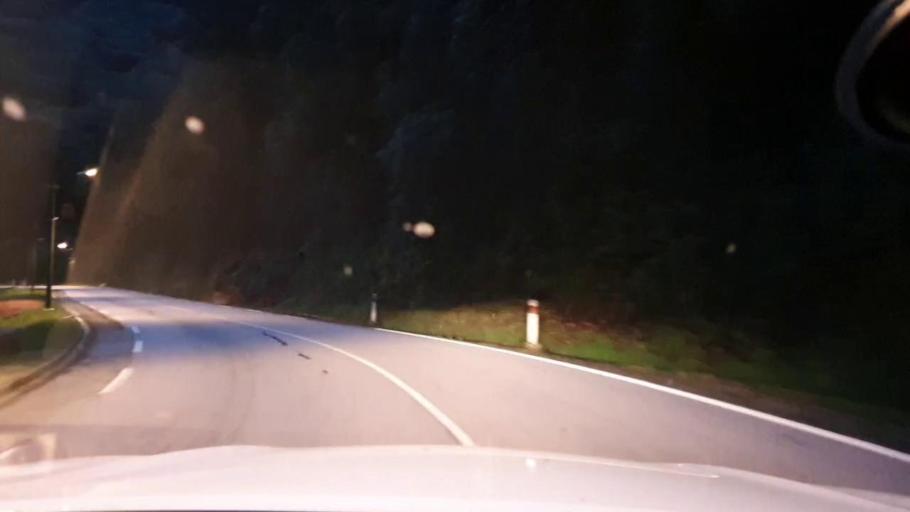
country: RW
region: Southern Province
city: Nzega
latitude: -2.5317
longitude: 29.3868
